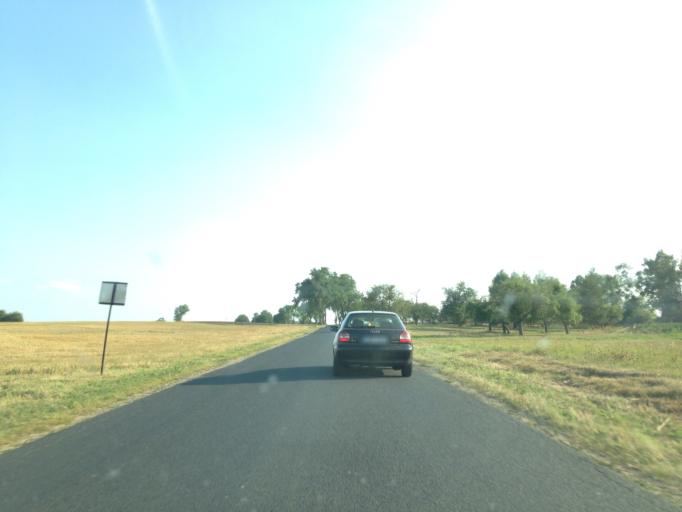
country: PL
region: Kujawsko-Pomorskie
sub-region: Powiat brodnicki
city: Brodnica
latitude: 53.3764
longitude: 19.3735
